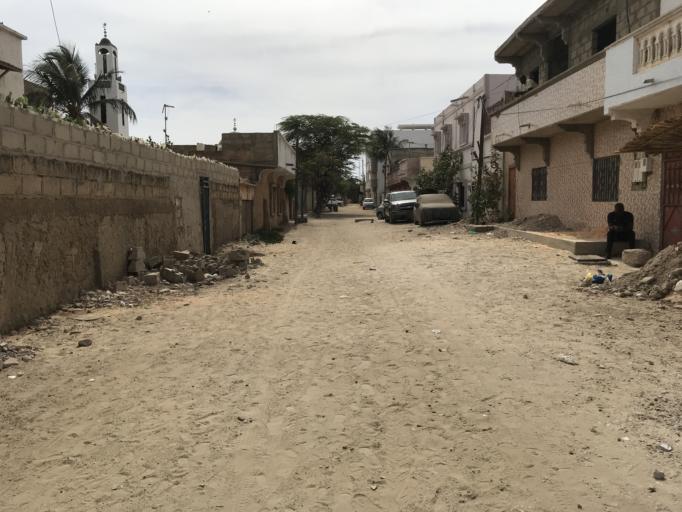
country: SN
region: Saint-Louis
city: Saint-Louis
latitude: 16.0246
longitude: -16.4858
